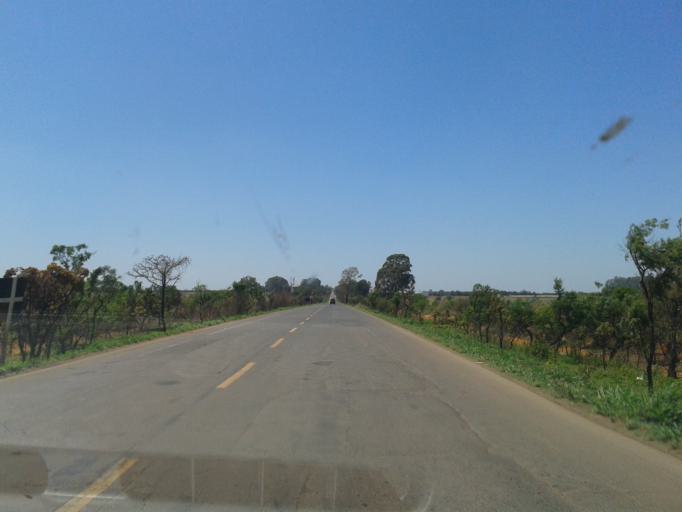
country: BR
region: Minas Gerais
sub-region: Araxa
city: Araxa
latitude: -19.4031
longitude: -47.3174
